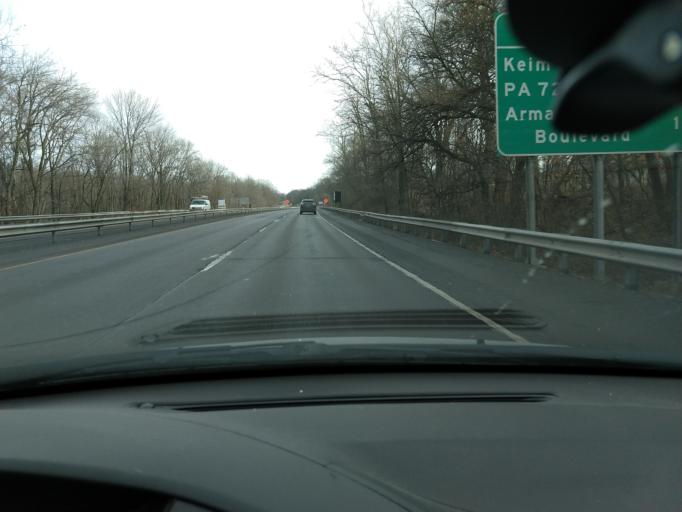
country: US
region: Pennsylvania
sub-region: Chester County
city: South Pottstown
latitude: 40.2361
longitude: -75.6459
